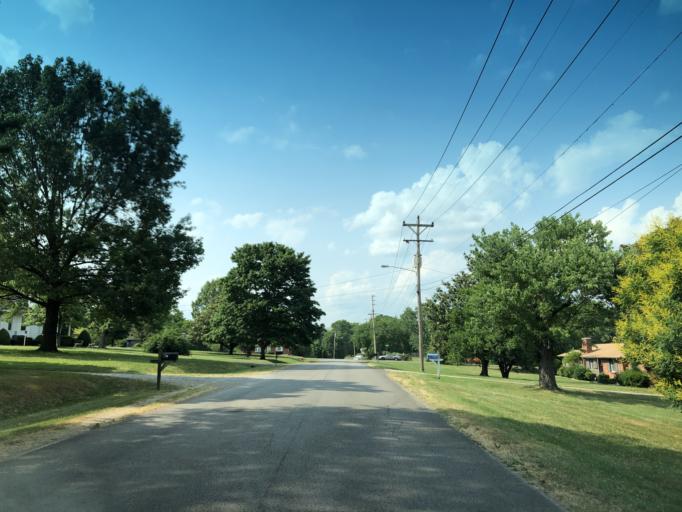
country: US
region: Tennessee
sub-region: Davidson County
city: Goodlettsville
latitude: 36.2603
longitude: -86.7213
